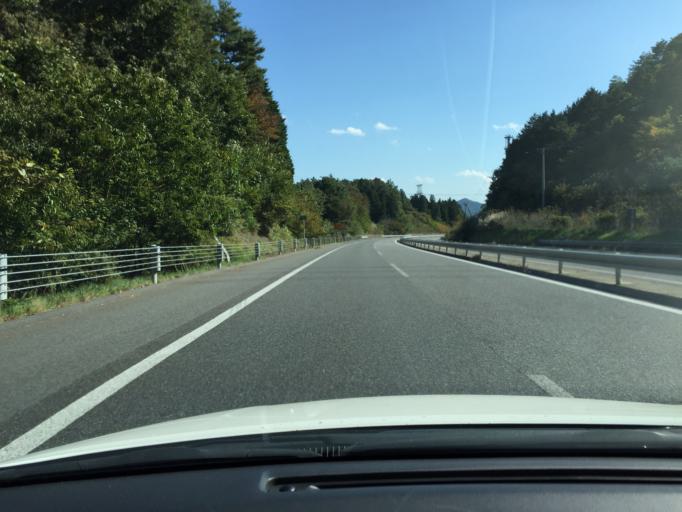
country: JP
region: Fukushima
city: Iwaki
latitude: 37.1638
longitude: 140.7292
